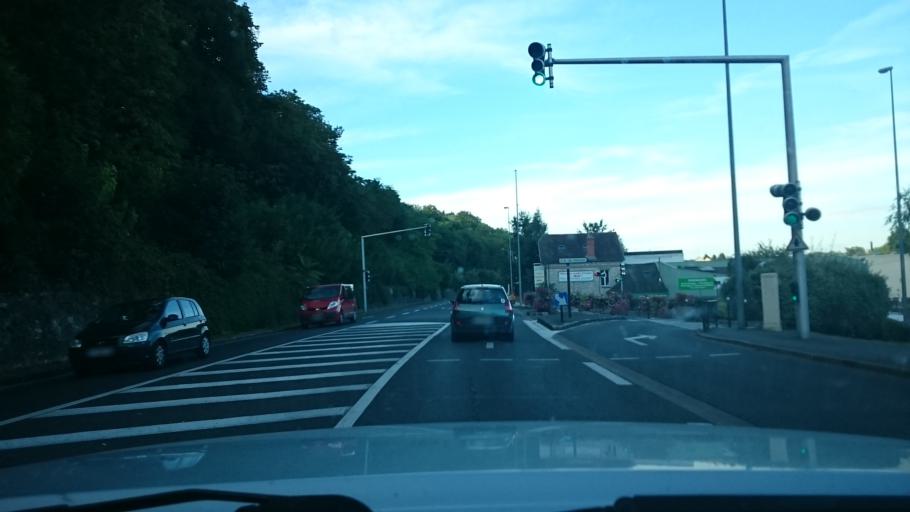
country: FR
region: Ile-de-France
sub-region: Departement de Seine-et-Marne
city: Samoreau
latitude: 48.4237
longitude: 2.7392
